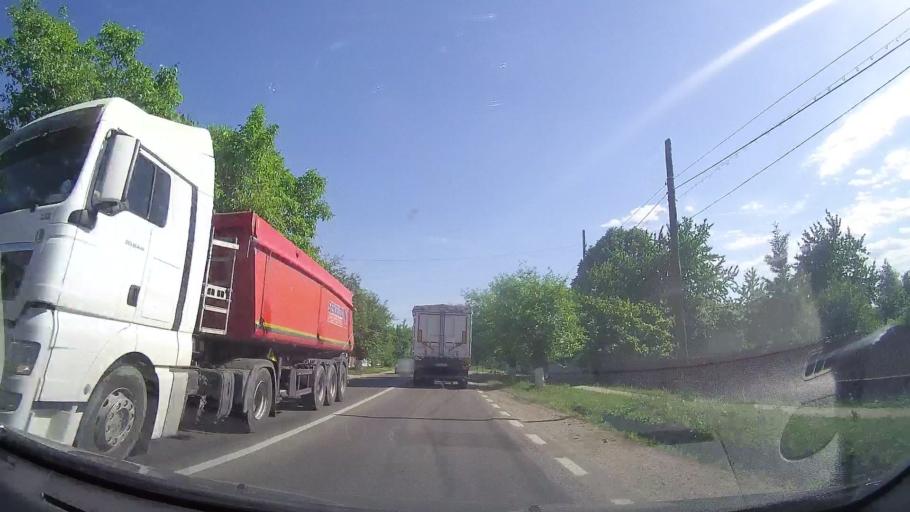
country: RO
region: Prahova
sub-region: Comuna Magurele
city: Magurele
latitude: 45.0936
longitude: 26.0368
